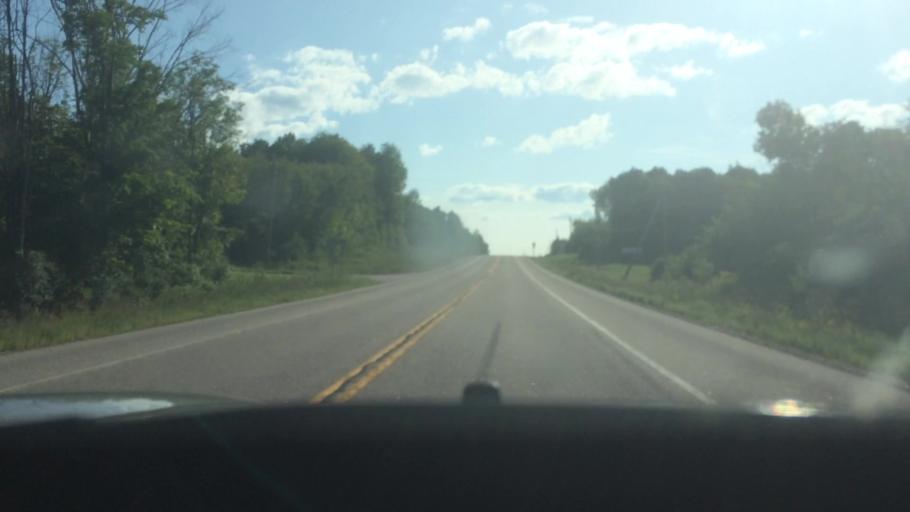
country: US
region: New York
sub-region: Franklin County
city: Malone
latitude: 44.7534
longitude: -74.5538
